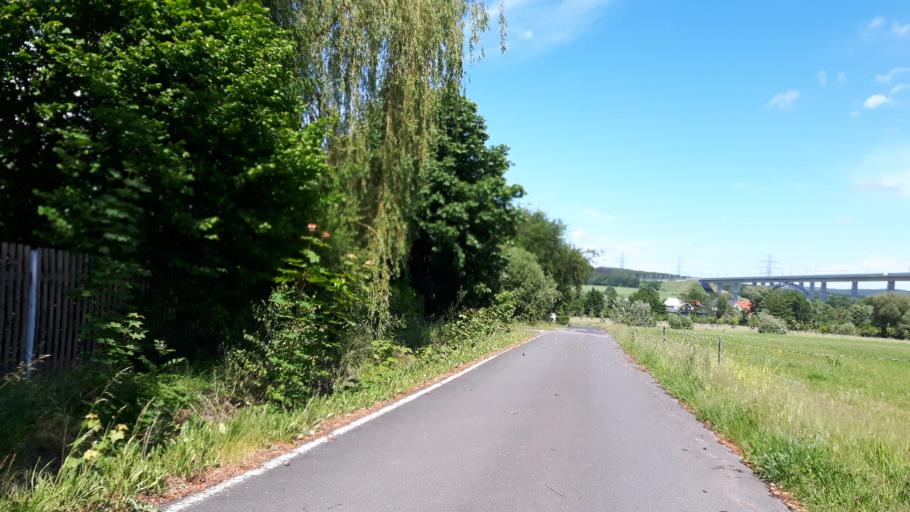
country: DE
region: Thuringia
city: Langewiesen
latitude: 50.6672
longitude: 10.9806
